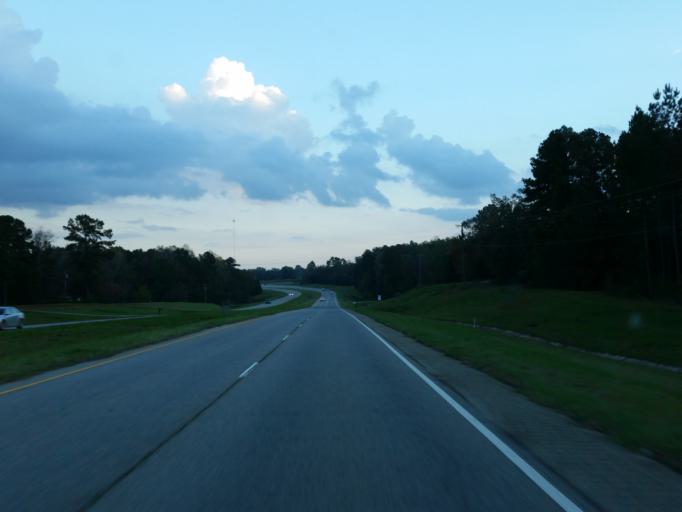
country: US
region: Georgia
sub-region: Pulaski County
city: Hawkinsville
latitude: 32.3328
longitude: -83.5641
